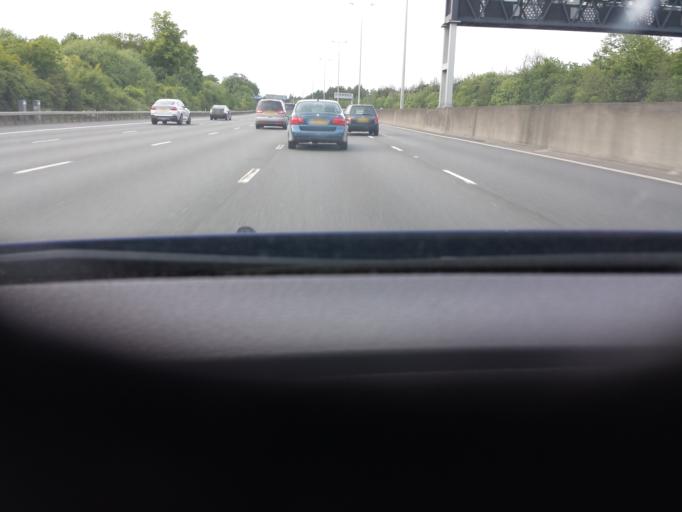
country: GB
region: England
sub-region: Surrey
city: Egham
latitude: 51.4151
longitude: -0.5403
